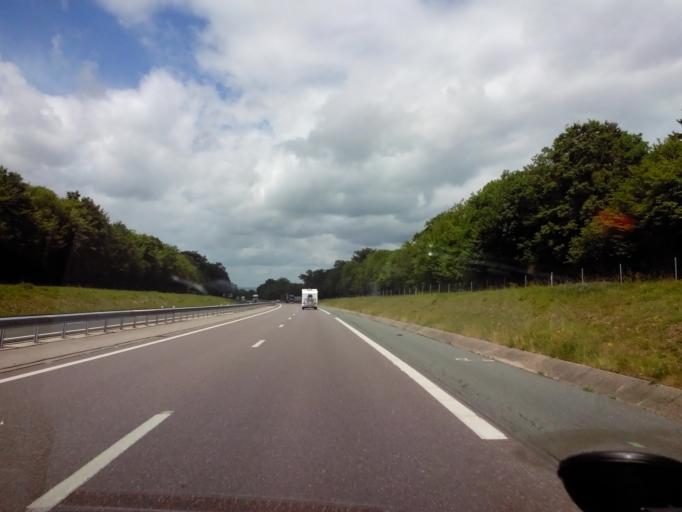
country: FR
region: Lorraine
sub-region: Departement de Meurthe-et-Moselle
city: Colombey-les-Belles
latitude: 48.5236
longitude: 5.9153
